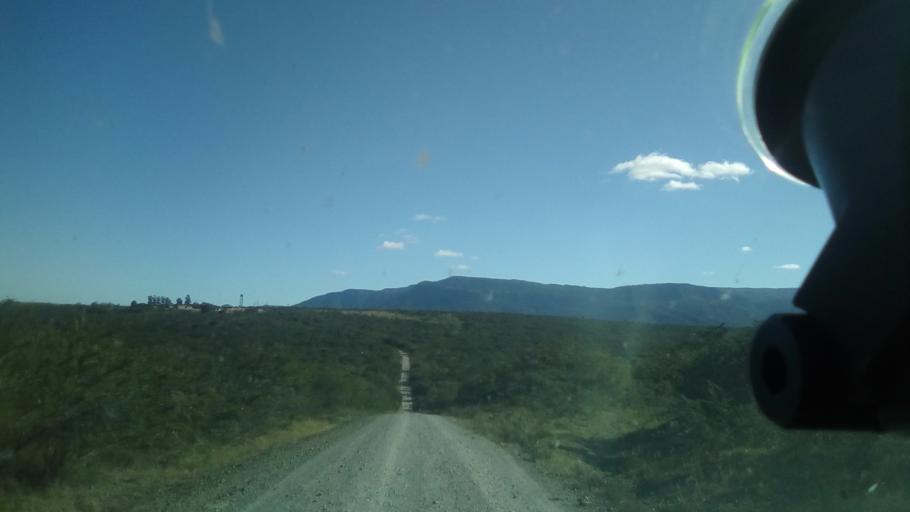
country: ZA
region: Eastern Cape
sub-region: Buffalo City Metropolitan Municipality
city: Bhisho
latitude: -32.7526
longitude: 27.3446
